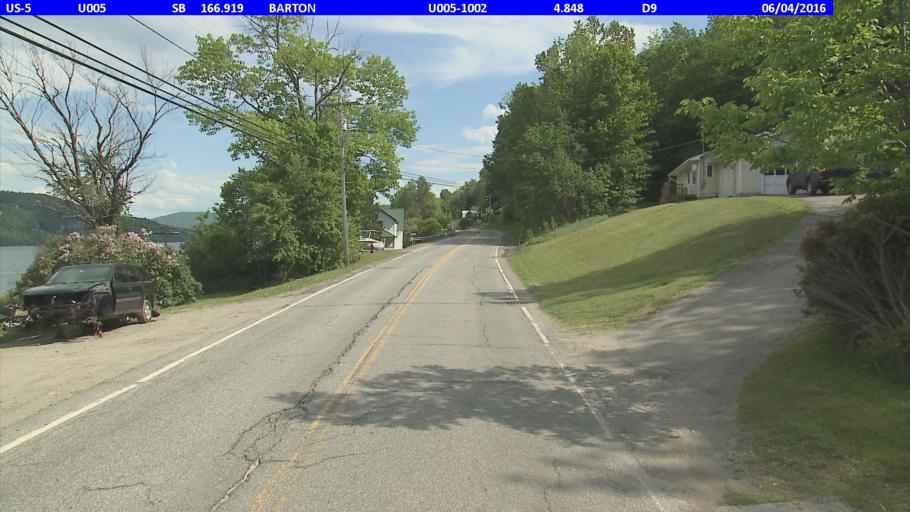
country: US
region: Vermont
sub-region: Orleans County
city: Newport
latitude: 44.7419
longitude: -72.1695
